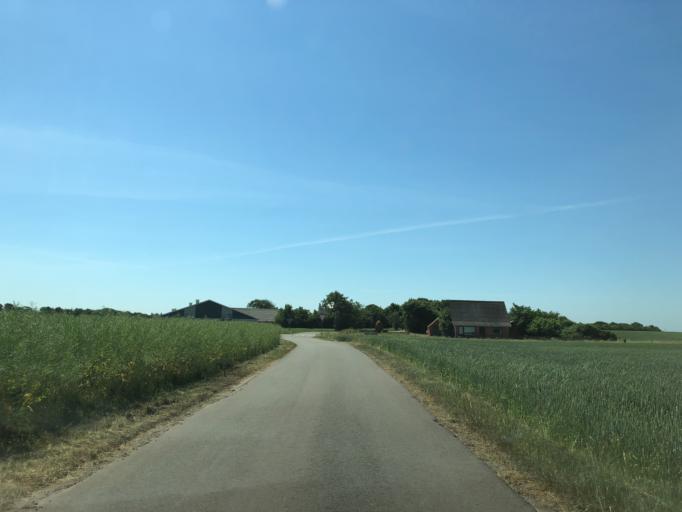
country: DK
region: Central Jutland
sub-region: Struer Kommune
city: Struer
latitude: 56.4236
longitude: 8.4383
